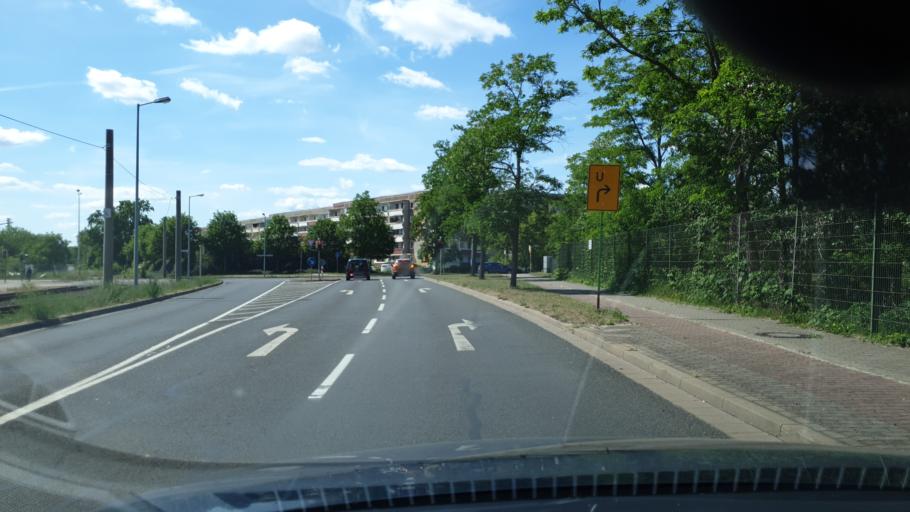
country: DE
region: Saxony-Anhalt
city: Dessau
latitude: 51.8141
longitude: 12.2507
